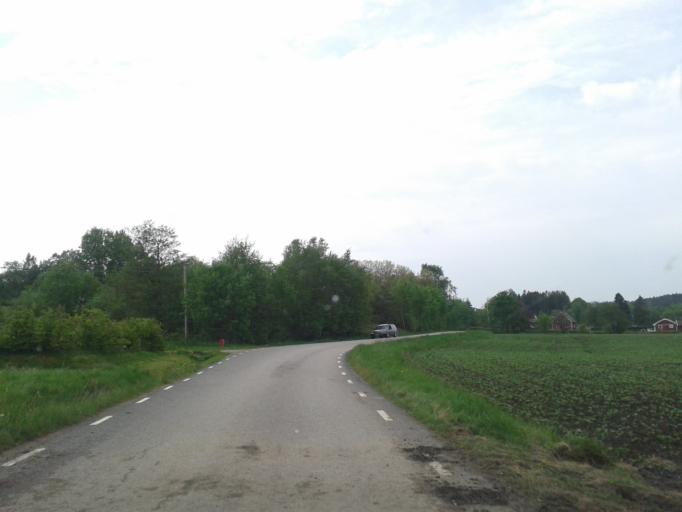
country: SE
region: Vaestra Goetaland
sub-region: Kungalvs Kommun
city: Kungalv
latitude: 57.9183
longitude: 11.9270
